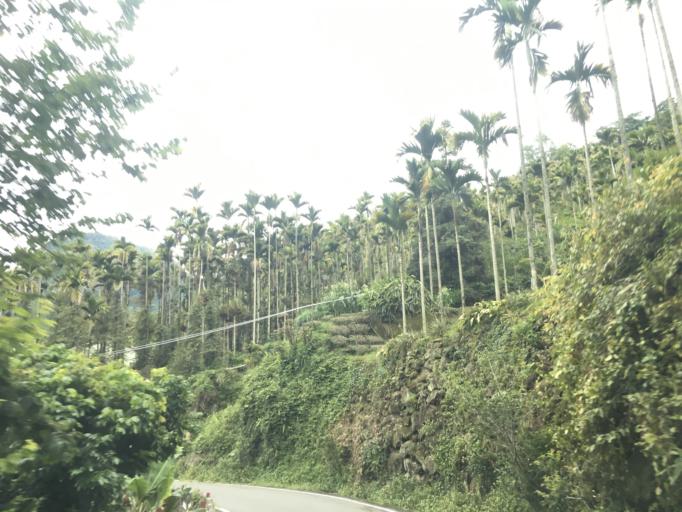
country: TW
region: Taiwan
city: Lugu
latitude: 23.5392
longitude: 120.7131
